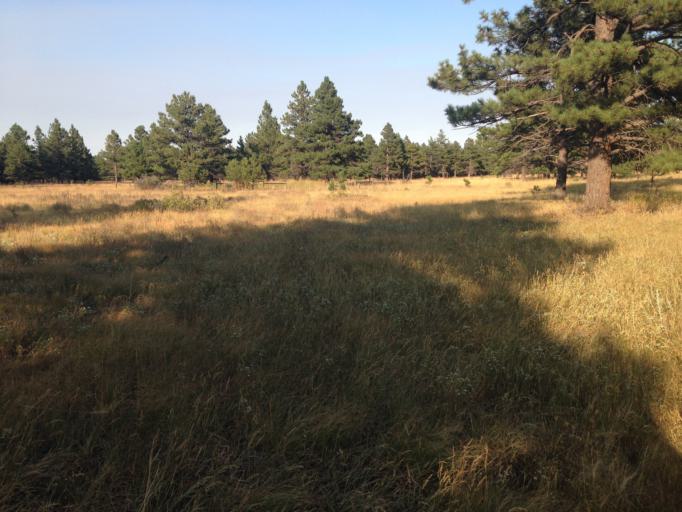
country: US
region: Colorado
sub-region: Boulder County
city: Superior
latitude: 39.9145
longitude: -105.2579
